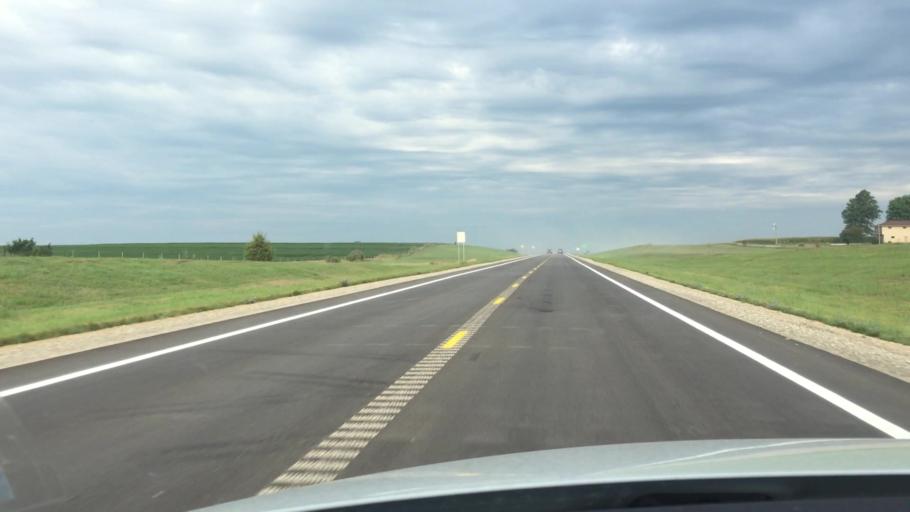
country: US
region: Kansas
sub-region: Doniphan County
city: Highland
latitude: 39.8412
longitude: -95.4020
